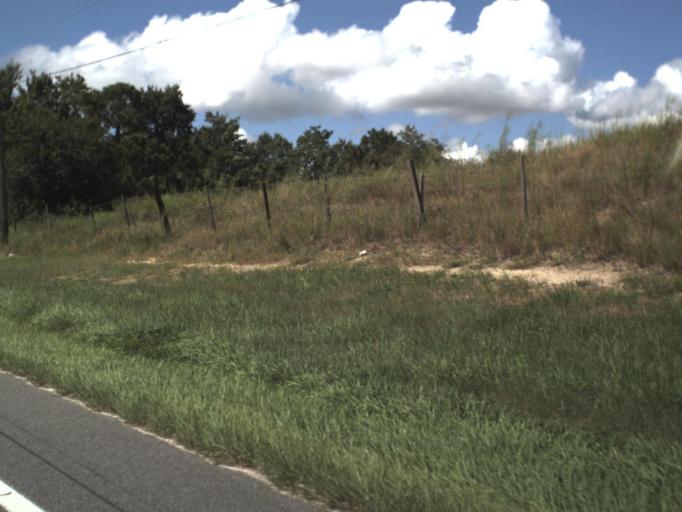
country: US
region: Florida
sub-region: Polk County
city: Loughman
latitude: 28.2291
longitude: -81.5639
